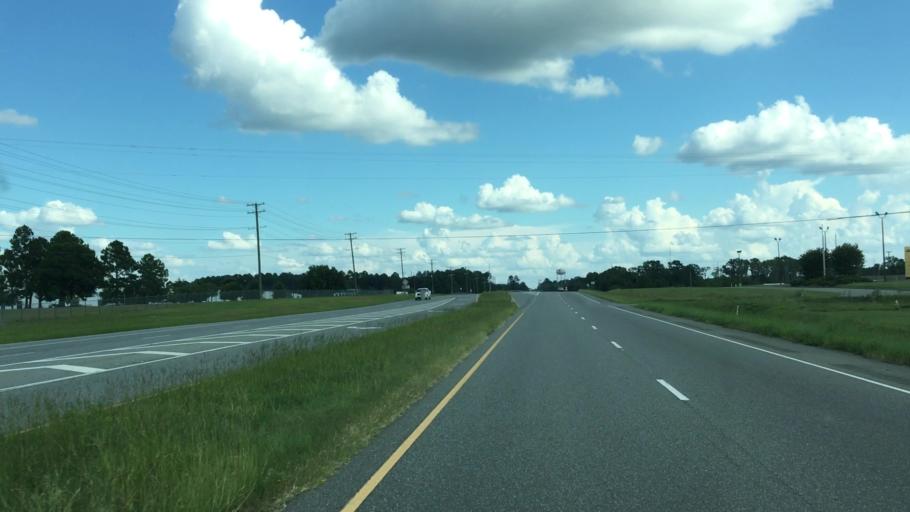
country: US
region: Georgia
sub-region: Laurens County
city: Dublin
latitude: 32.5093
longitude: -82.9492
